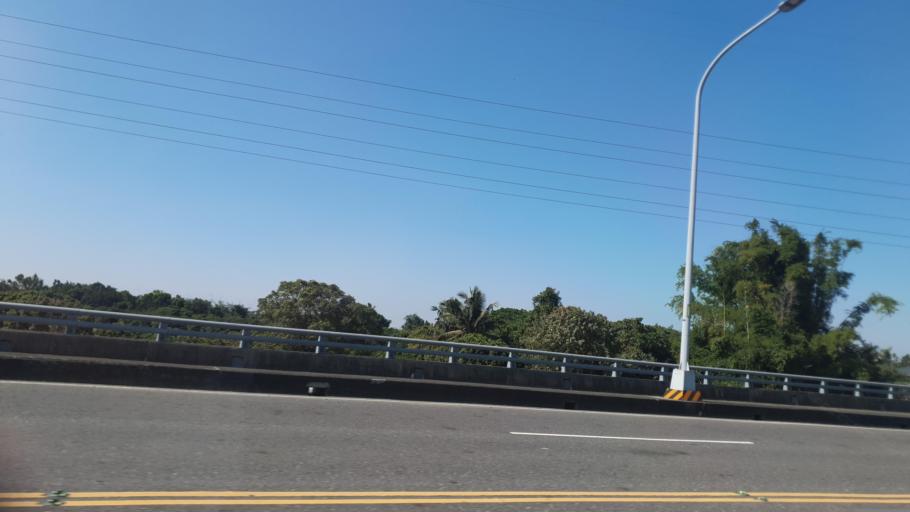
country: TW
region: Taiwan
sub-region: Tainan
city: Tainan
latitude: 23.0344
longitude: 120.3220
